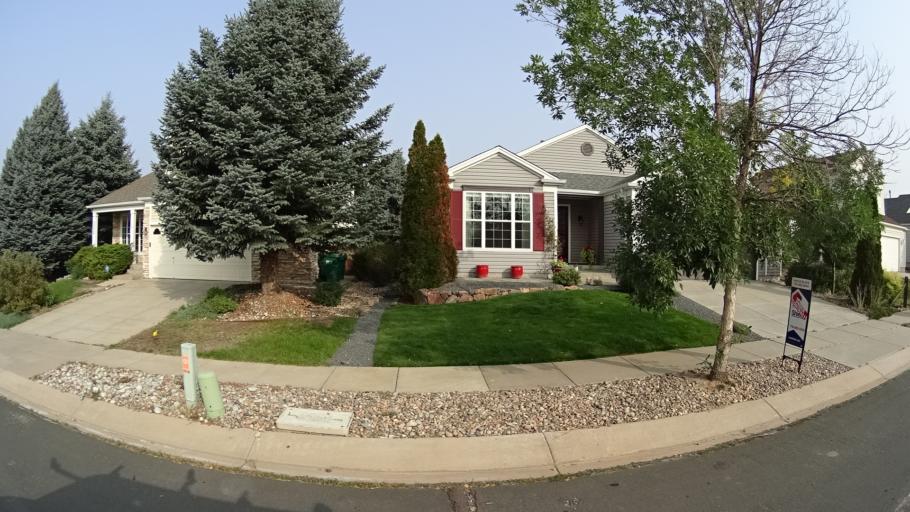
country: US
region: Colorado
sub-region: El Paso County
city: Cimarron Hills
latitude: 38.9313
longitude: -104.7282
